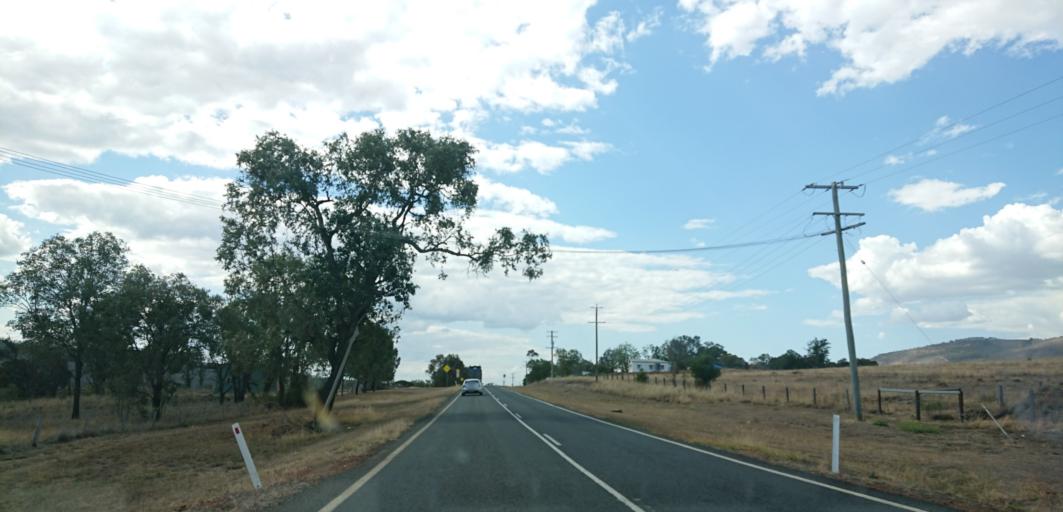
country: AU
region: Queensland
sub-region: Lockyer Valley
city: Gatton
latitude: -27.6672
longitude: 152.1585
